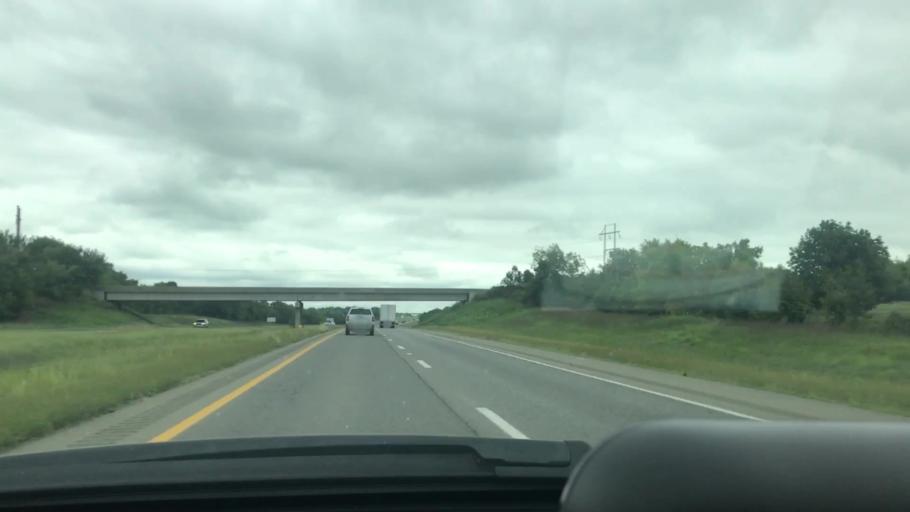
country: US
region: Oklahoma
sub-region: McIntosh County
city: Checotah
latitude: 35.3899
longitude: -95.5660
